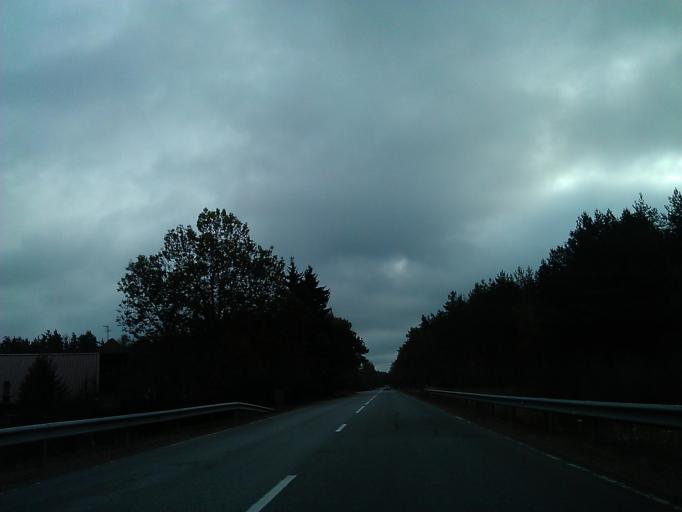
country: LV
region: Ikskile
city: Ikskile
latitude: 56.8921
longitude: 24.4552
